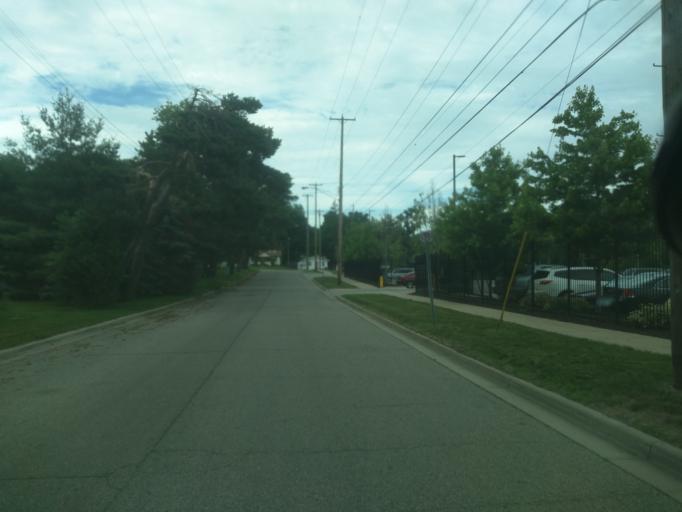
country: US
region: Michigan
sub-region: Ingham County
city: Lansing
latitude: 42.6888
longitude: -84.5345
